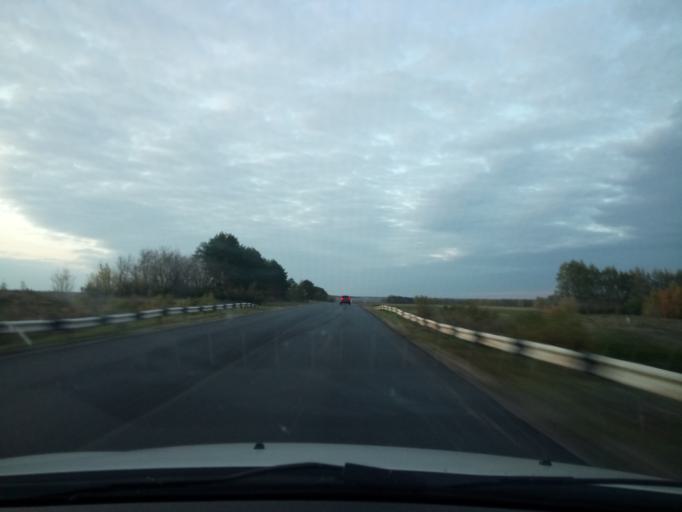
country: RU
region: Nizjnij Novgorod
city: Bol'shoye Murashkino
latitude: 55.8572
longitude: 44.7492
